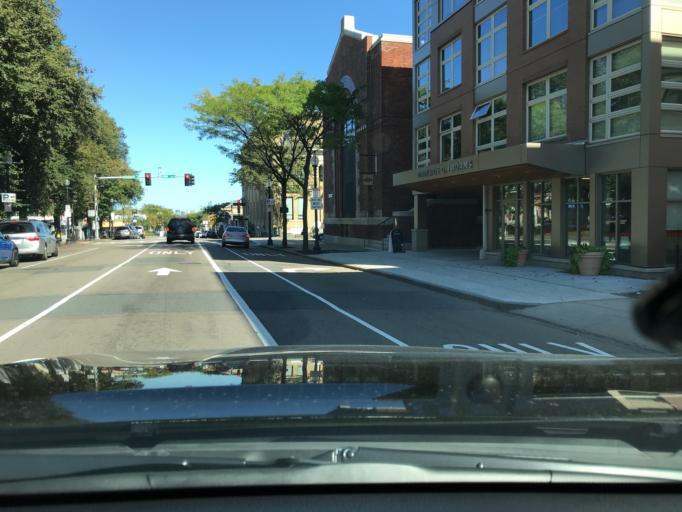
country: US
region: Massachusetts
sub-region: Suffolk County
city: Jamaica Plain
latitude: 42.2861
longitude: -71.1285
